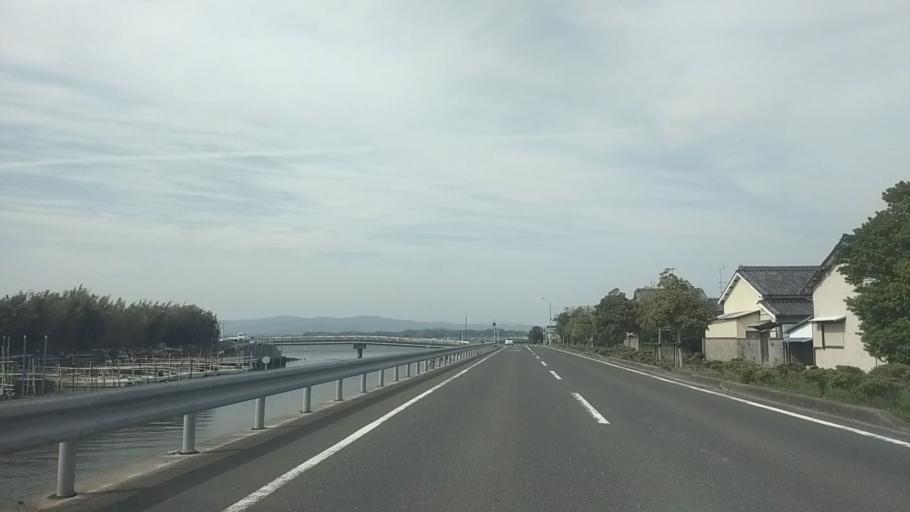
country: JP
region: Shizuoka
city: Kosai-shi
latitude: 34.7118
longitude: 137.6193
